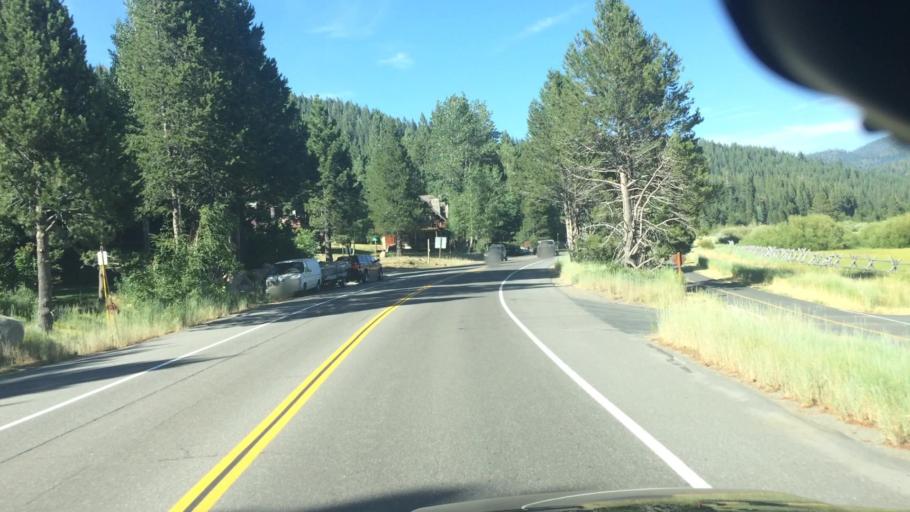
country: US
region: California
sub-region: Placer County
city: Sunnyside-Tahoe City
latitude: 39.2018
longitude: -120.2241
